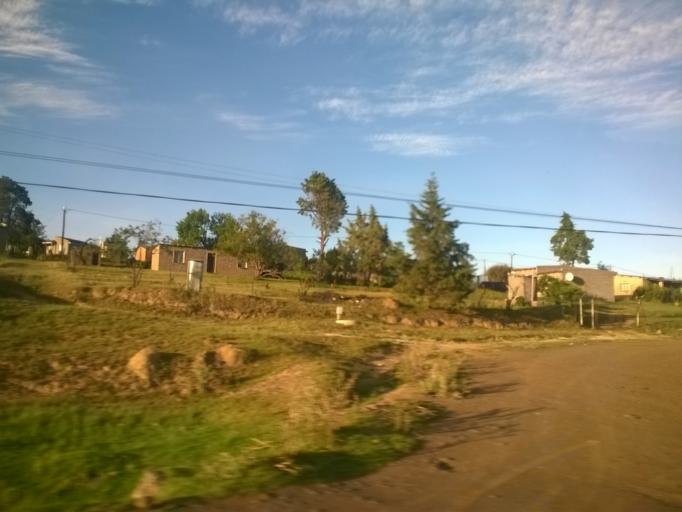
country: LS
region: Berea
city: Teyateyaneng
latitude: -29.1502
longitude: 27.7331
